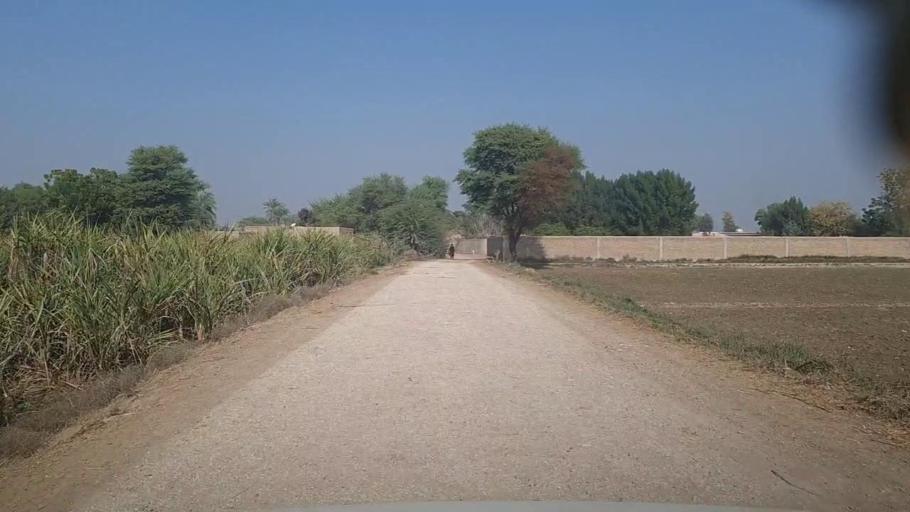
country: PK
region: Sindh
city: Karaundi
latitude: 26.9761
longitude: 68.4501
